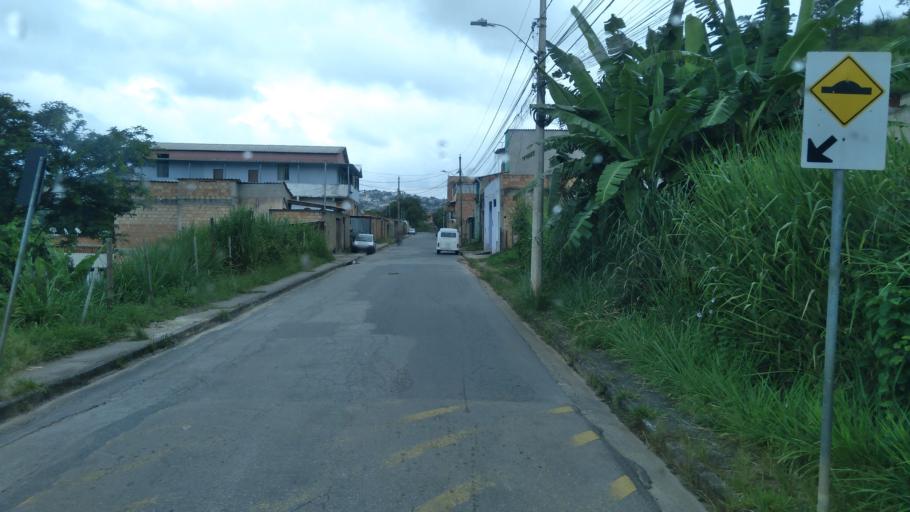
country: BR
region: Minas Gerais
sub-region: Santa Luzia
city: Santa Luzia
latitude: -19.8373
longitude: -43.8700
